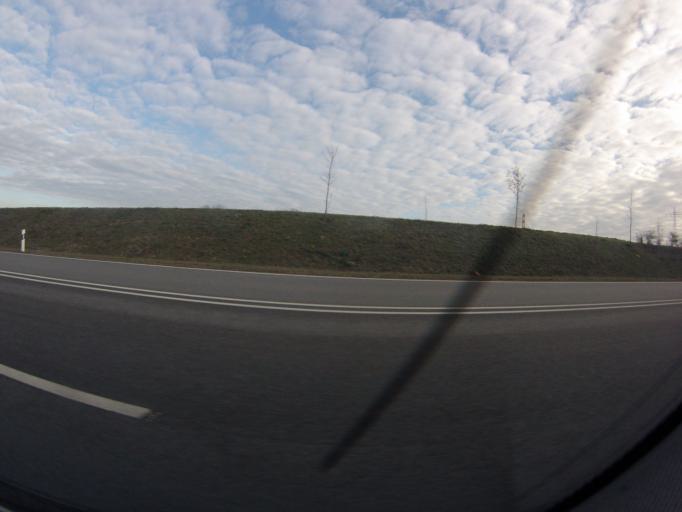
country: DE
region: Thuringia
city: Gossnitz
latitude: 50.8971
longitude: 12.4442
